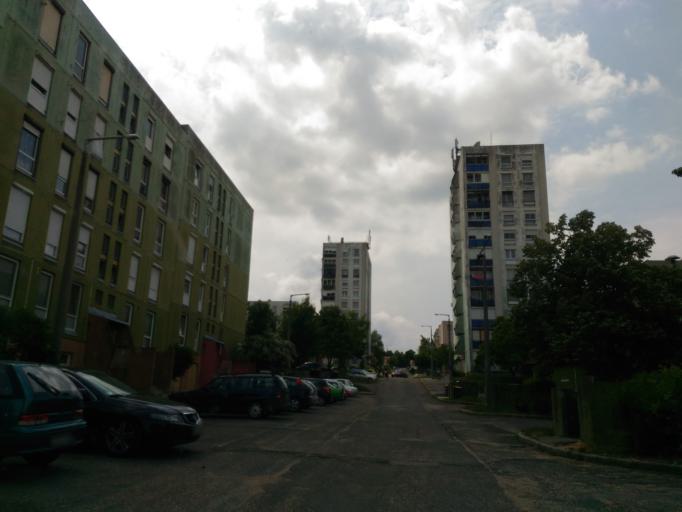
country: HU
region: Baranya
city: Komlo
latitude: 46.1892
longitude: 18.2326
